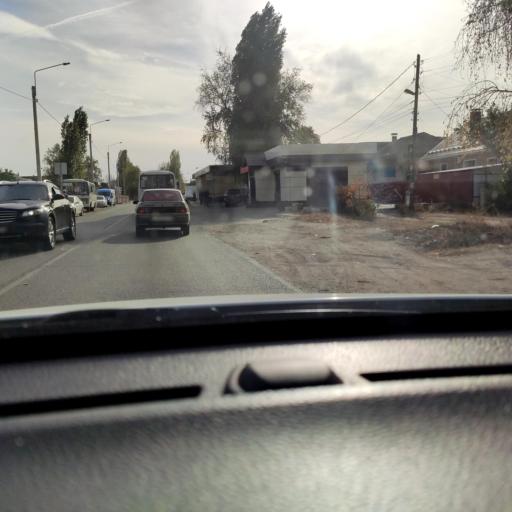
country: RU
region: Voronezj
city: Maslovka
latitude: 51.5507
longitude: 39.2350
